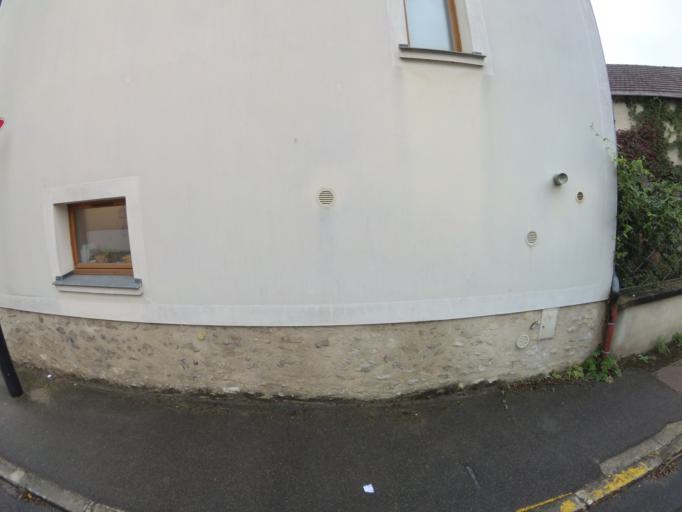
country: FR
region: Ile-de-France
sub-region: Departement de Seine-et-Marne
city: Bussy-Saint-Georges
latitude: 48.8457
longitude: 2.6956
